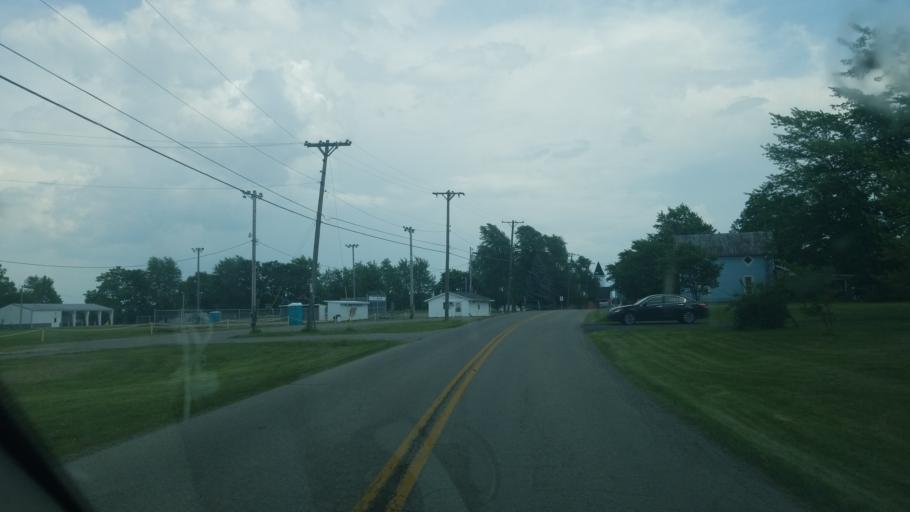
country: US
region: Ohio
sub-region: Logan County
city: Northwood
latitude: 40.4633
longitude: -83.6756
